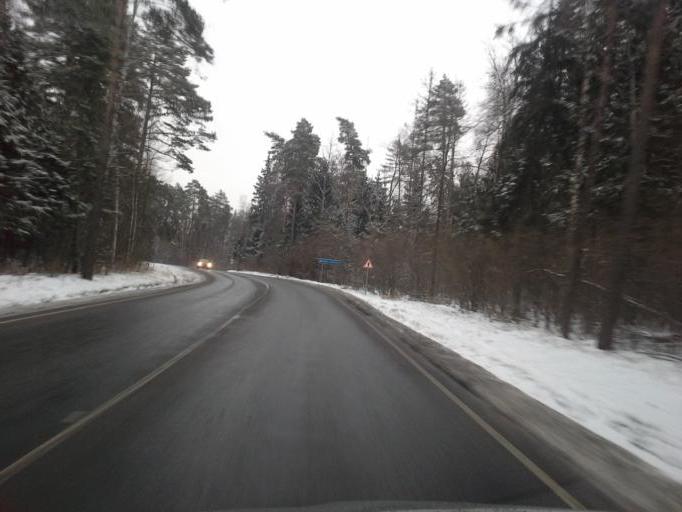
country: RU
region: Moskovskaya
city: Zhavoronki
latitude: 55.7036
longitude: 37.1039
